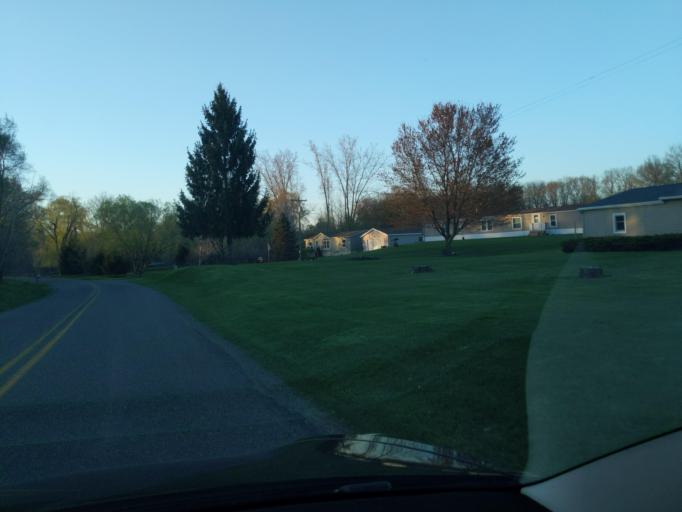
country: US
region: Michigan
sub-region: Ingham County
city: Stockbridge
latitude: 42.4937
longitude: -84.2944
